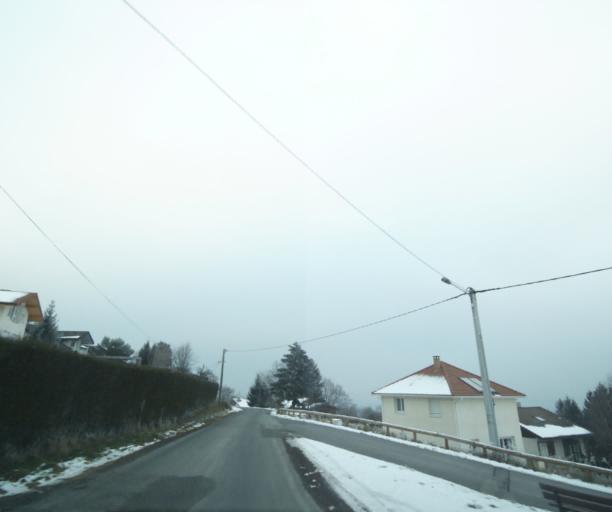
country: FR
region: Rhone-Alpes
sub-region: Departement de la Haute-Savoie
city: Reignier-Esery
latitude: 46.1266
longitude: 6.2446
